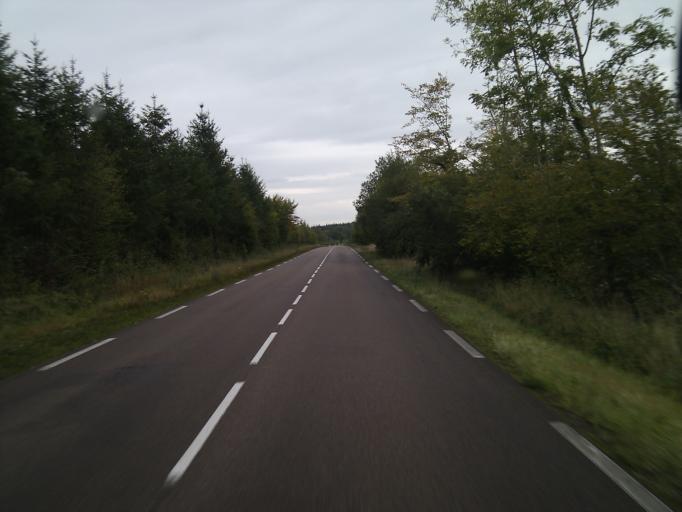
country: FR
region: Bourgogne
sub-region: Departement de la Cote-d'Or
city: Saulieu
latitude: 47.3042
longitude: 4.2531
